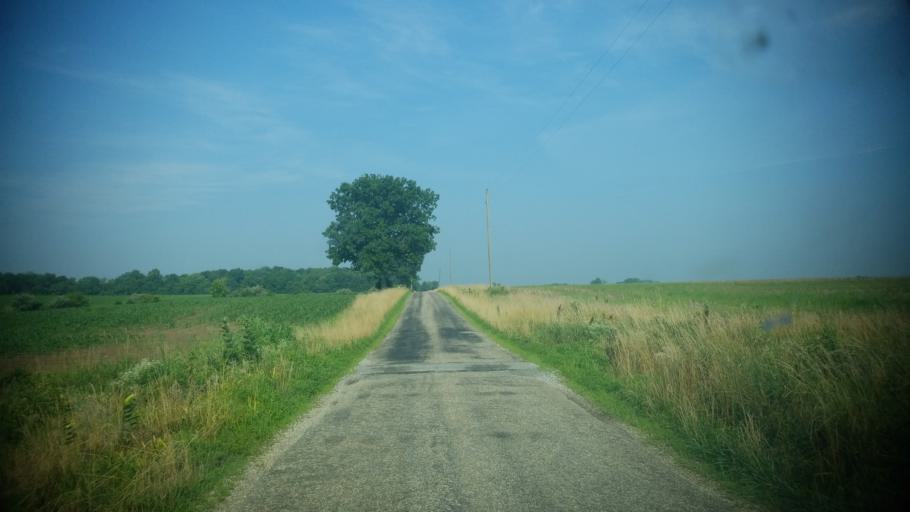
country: US
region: Illinois
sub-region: Clay County
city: Flora
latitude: 38.6030
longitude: -88.4251
